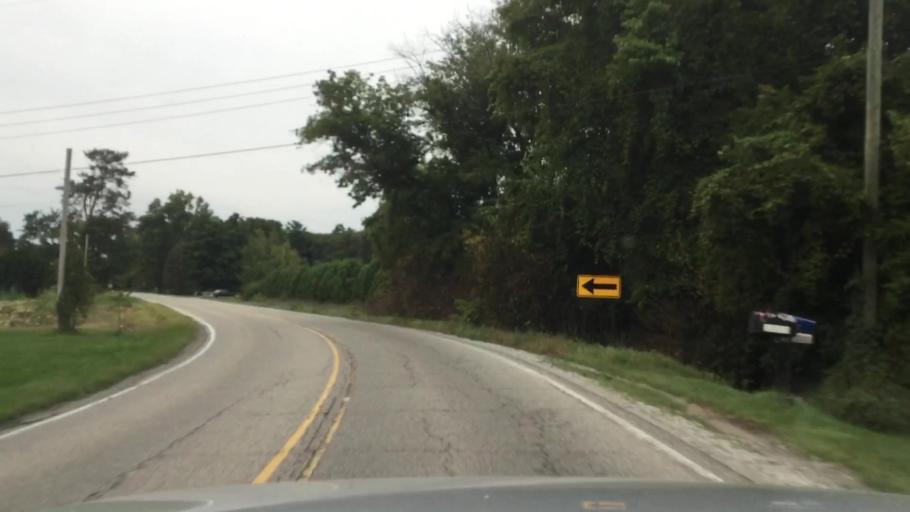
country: US
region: Michigan
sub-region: Washtenaw County
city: Milan
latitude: 42.1106
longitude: -83.7260
